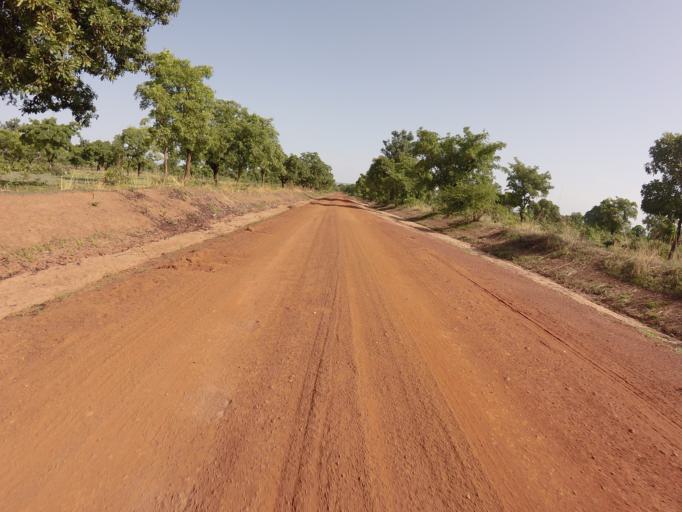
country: GH
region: Upper East
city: Bawku
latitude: 10.7453
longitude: -0.2004
